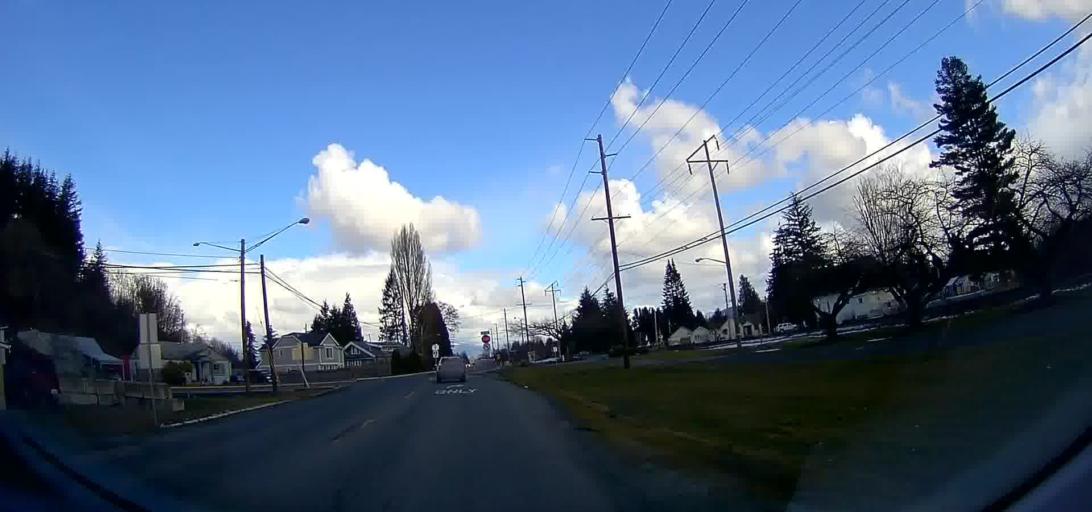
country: US
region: Washington
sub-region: Skagit County
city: Burlington
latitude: 48.4775
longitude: -122.3233
